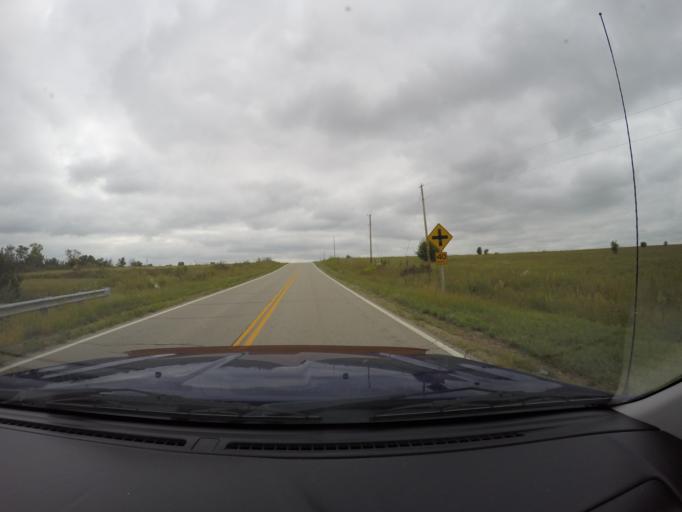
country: US
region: Kansas
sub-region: Morris County
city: Council Grove
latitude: 38.7977
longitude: -96.6840
